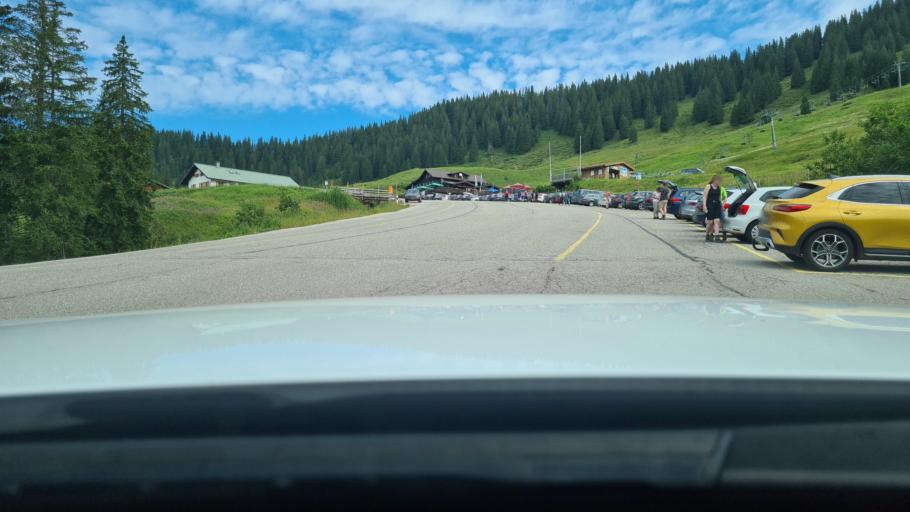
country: DE
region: Bavaria
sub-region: Swabia
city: Obermaiselstein
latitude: 47.4413
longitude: 10.1762
